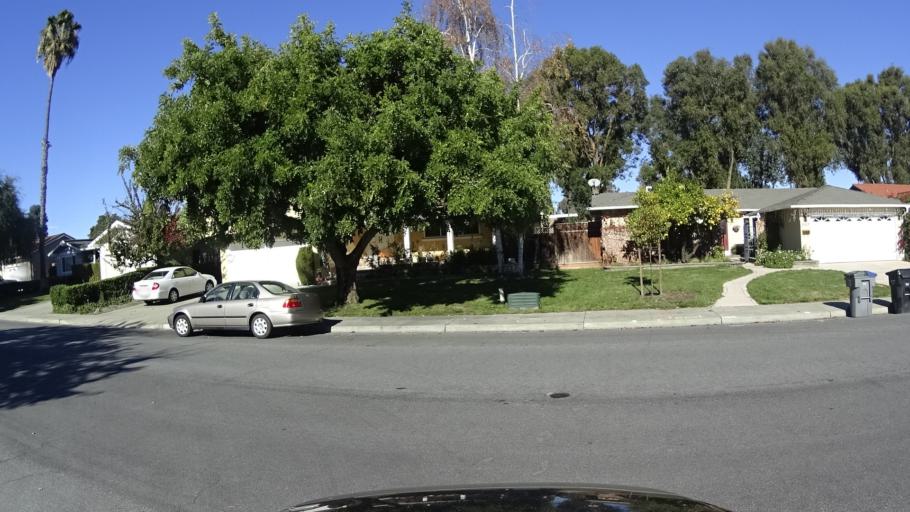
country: US
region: California
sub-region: Santa Clara County
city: Sunnyvale
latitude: 37.3508
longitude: -122.0025
